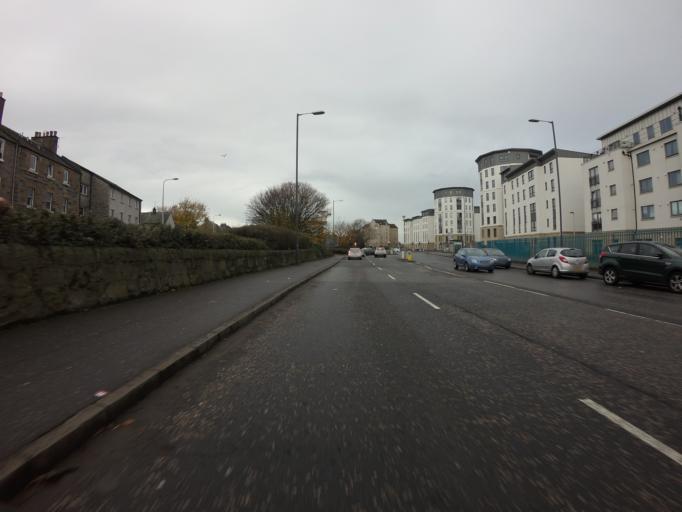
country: GB
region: Scotland
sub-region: Edinburgh
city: Edinburgh
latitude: 55.9800
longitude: -3.1897
